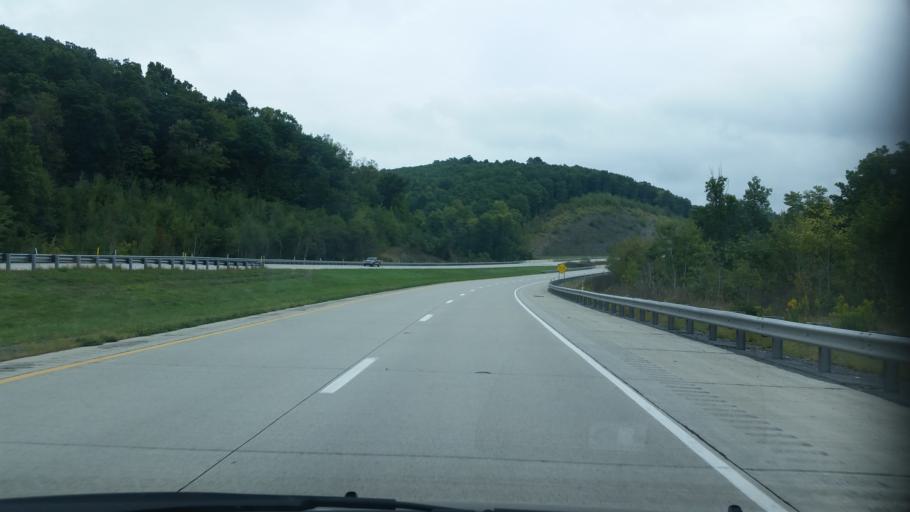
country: US
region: Pennsylvania
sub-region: Centre County
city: Stormstown
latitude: 40.8114
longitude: -78.0703
